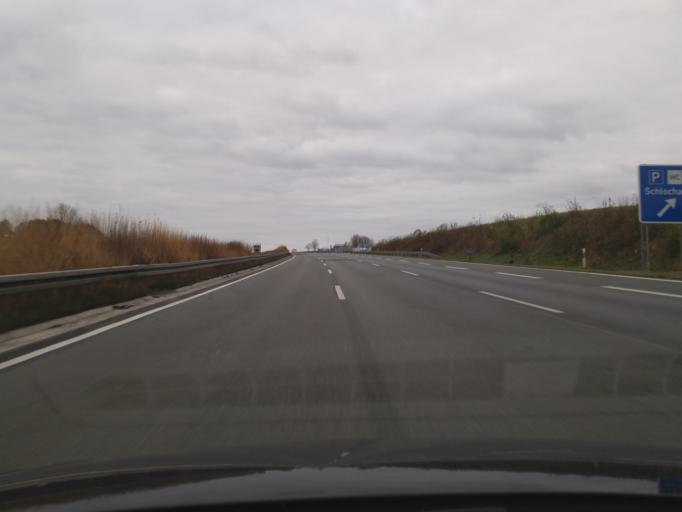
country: DE
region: Lower Saxony
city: Hillerse
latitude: 51.7191
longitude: 9.9441
